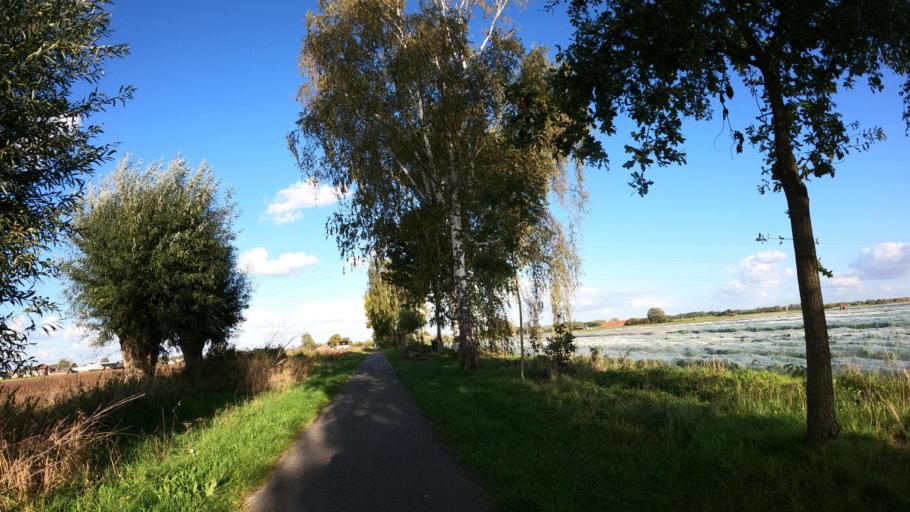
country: BE
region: Flanders
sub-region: Provincie Vlaams-Brabant
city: Merchtem
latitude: 50.9880
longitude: 4.2369
